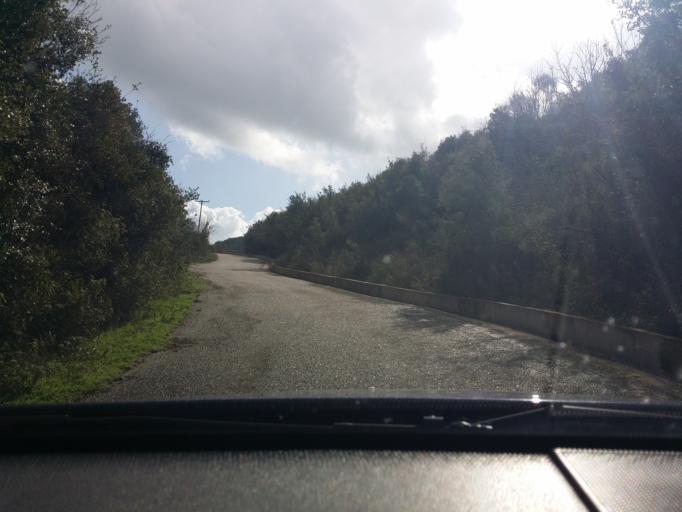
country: GR
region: West Greece
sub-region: Nomos Aitolias kai Akarnanias
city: Fitiai
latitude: 38.6628
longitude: 21.1919
